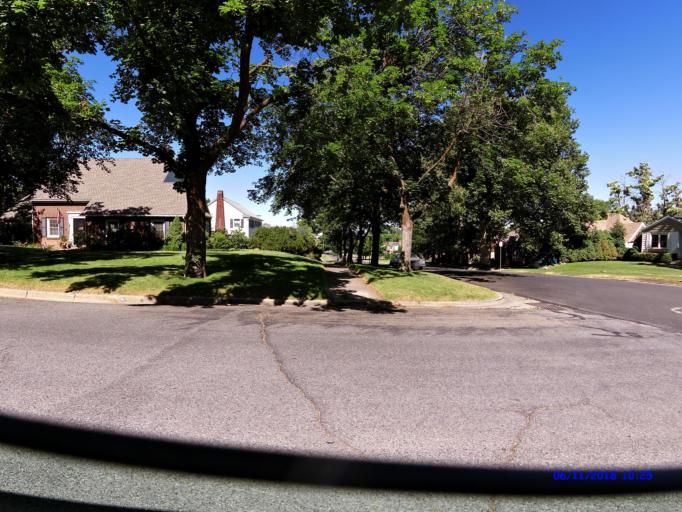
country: US
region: Utah
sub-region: Weber County
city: Ogden
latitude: 41.2149
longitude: -111.9428
